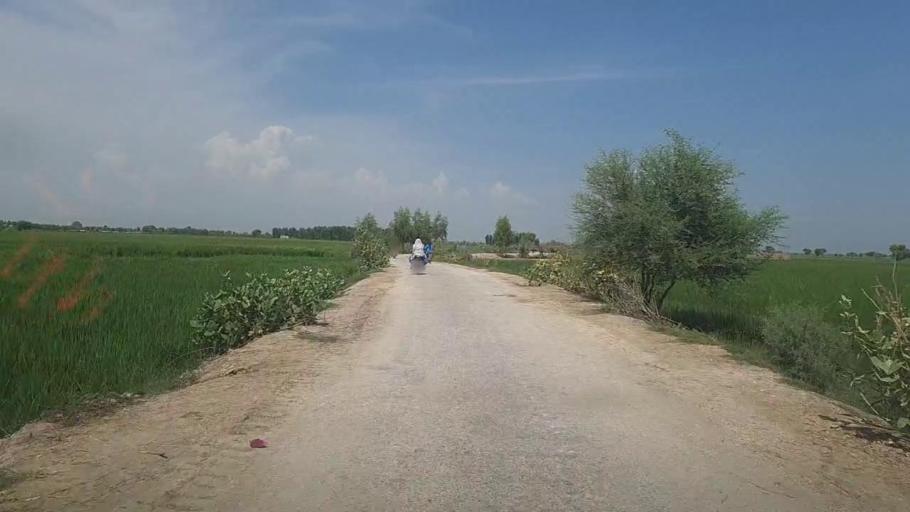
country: PK
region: Sindh
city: Kandhkot
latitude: 28.2860
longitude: 69.2372
